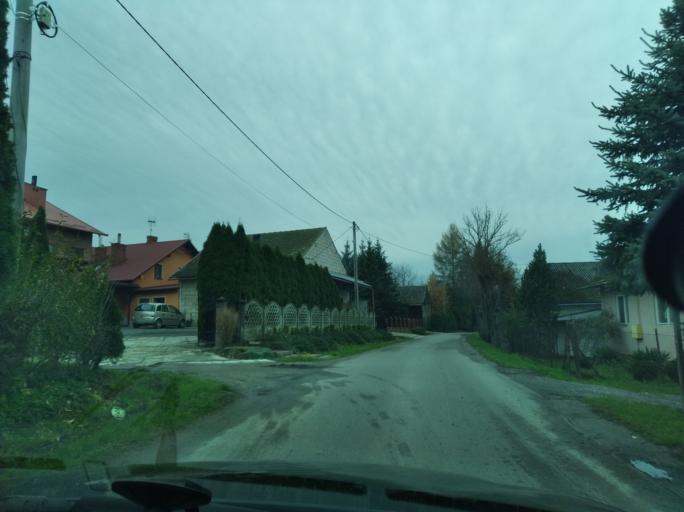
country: PL
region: Subcarpathian Voivodeship
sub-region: Powiat lancucki
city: Markowa
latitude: 50.0236
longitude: 22.3310
